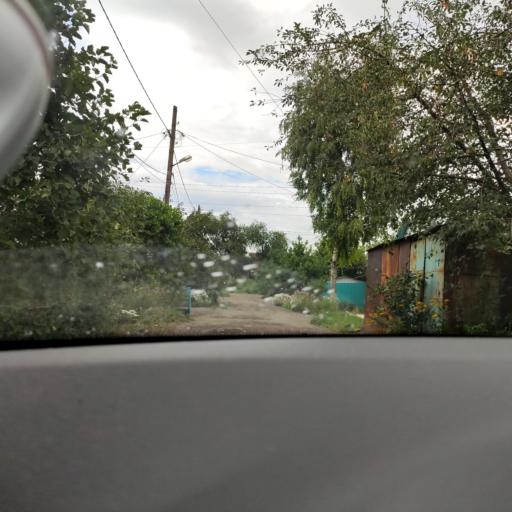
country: RU
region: Samara
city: Samara
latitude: 53.1857
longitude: 50.2369
